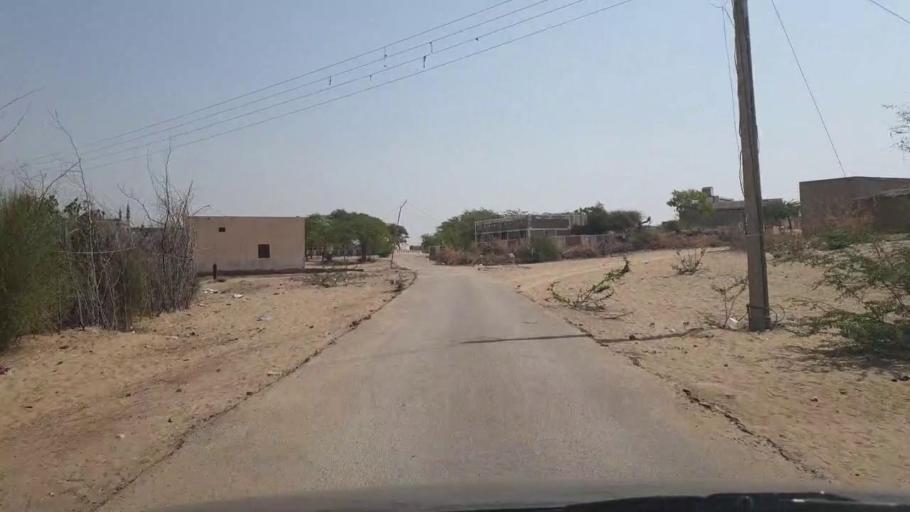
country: PK
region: Sindh
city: Chor
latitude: 25.6983
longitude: 70.2010
